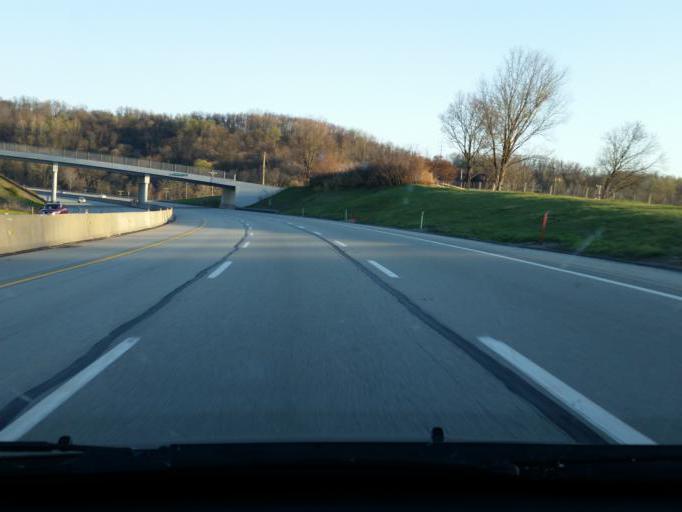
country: US
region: Pennsylvania
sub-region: Westmoreland County
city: Irwin
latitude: 40.2697
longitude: -79.6681
